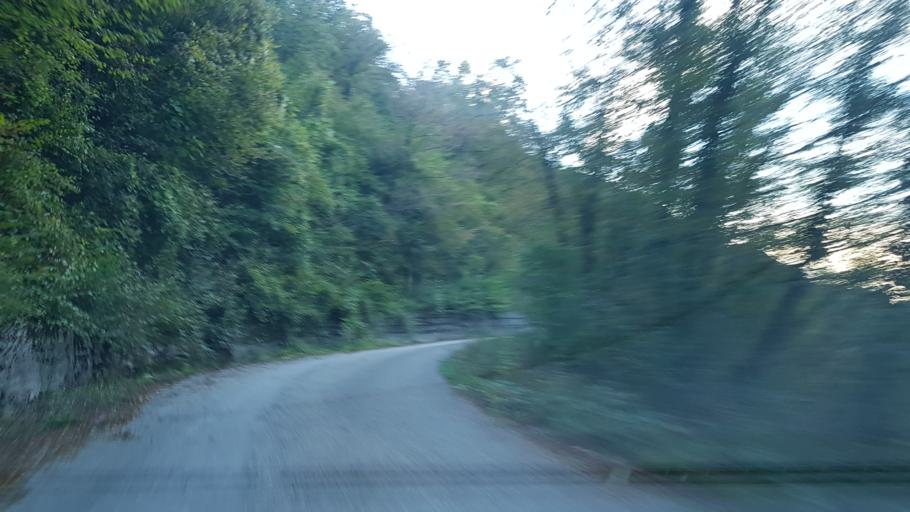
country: IT
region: Friuli Venezia Giulia
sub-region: Provincia di Udine
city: Venzone
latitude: 46.3350
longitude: 13.1613
